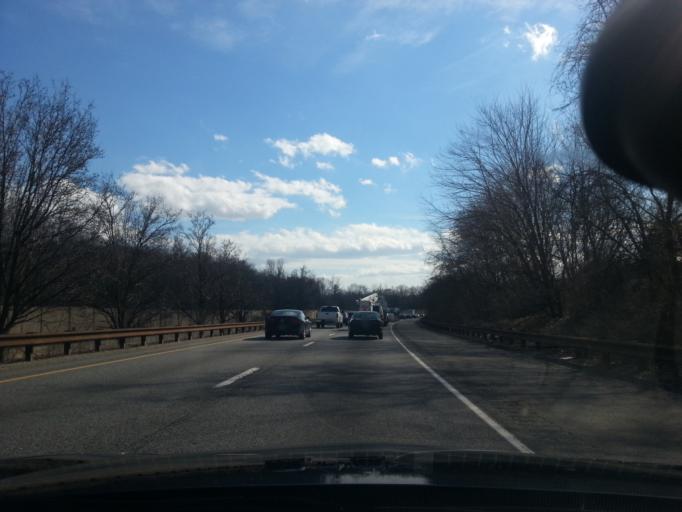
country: US
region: Pennsylvania
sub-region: Delaware County
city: Broomall
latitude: 39.9605
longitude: -75.3340
